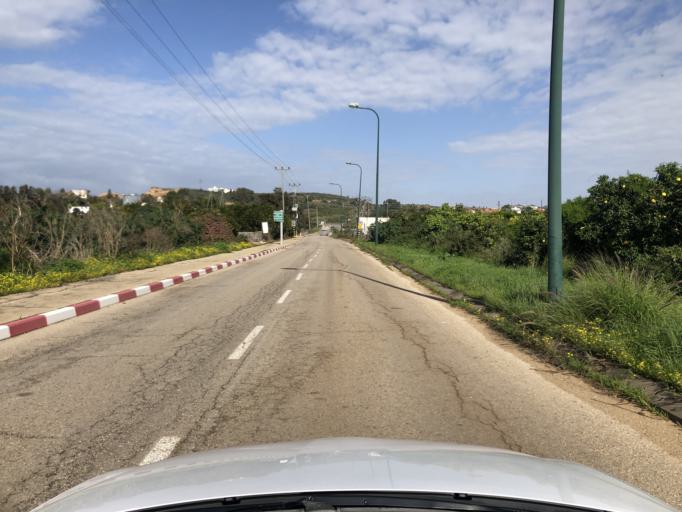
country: IL
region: Central District
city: Ness Ziona
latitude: 31.9178
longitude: 34.7787
